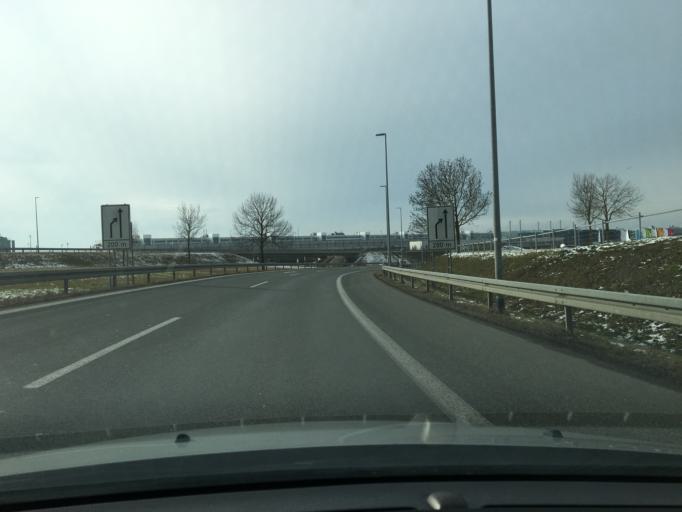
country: DE
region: Bavaria
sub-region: Upper Bavaria
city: Hallbergmoos
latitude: 48.3552
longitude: 11.7741
